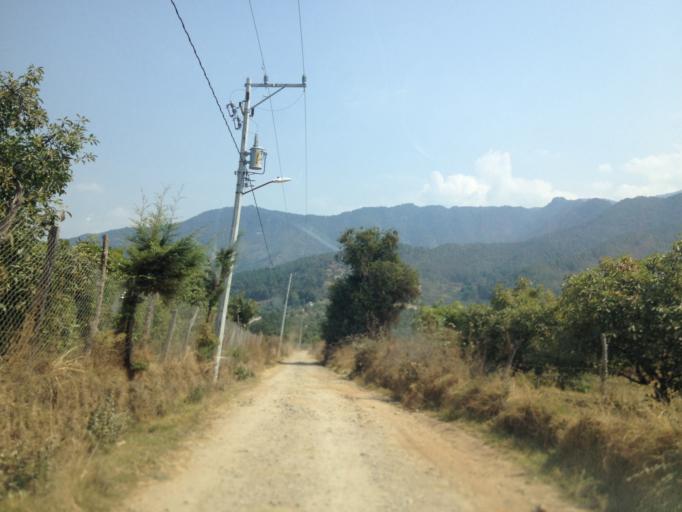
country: MX
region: Michoacan
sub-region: Zitacuaro
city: Macutzio
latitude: 19.4888
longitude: -100.3307
